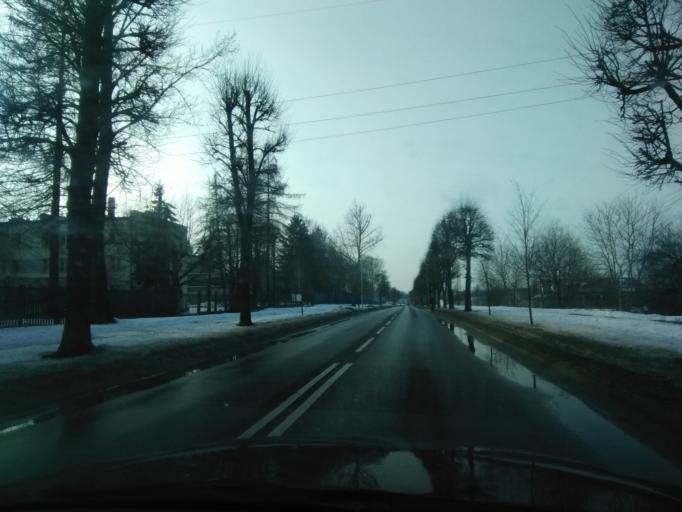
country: PL
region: Subcarpathian Voivodeship
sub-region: Krosno
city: Krosno
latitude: 49.7010
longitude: 21.7401
